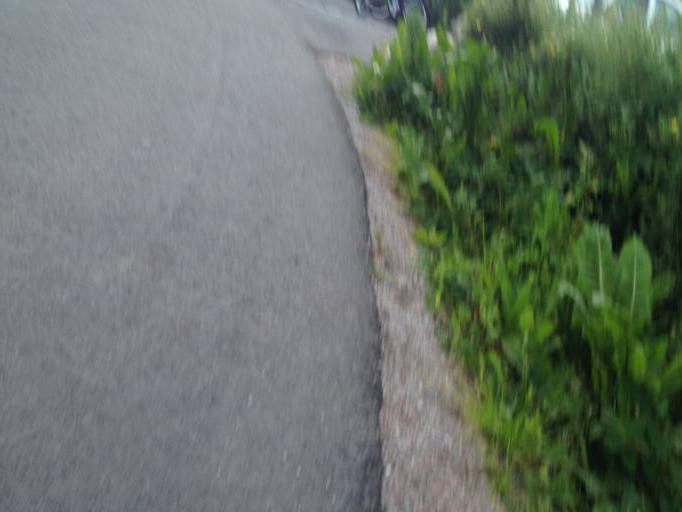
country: SE
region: Stockholm
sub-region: Sigtuna Kommun
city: Marsta
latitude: 59.6159
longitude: 17.8462
